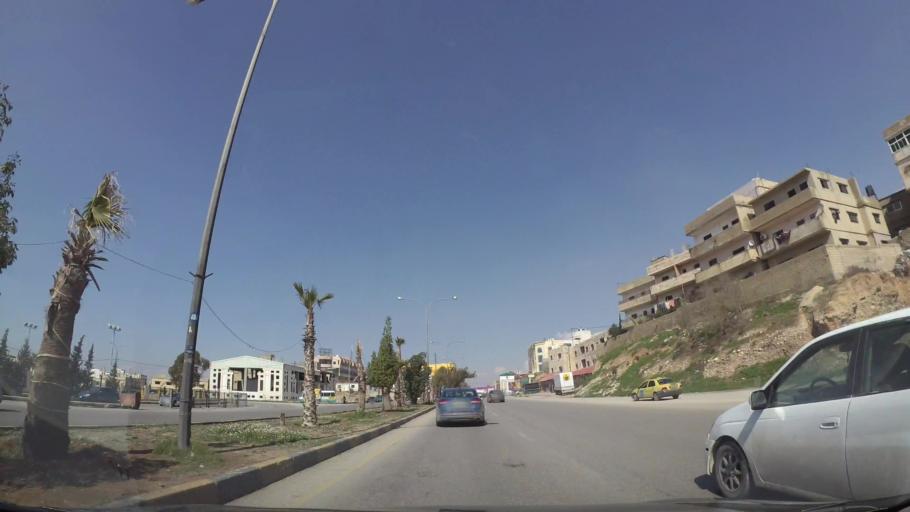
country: JO
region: Zarqa
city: Zarqa
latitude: 32.0309
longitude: 36.0890
